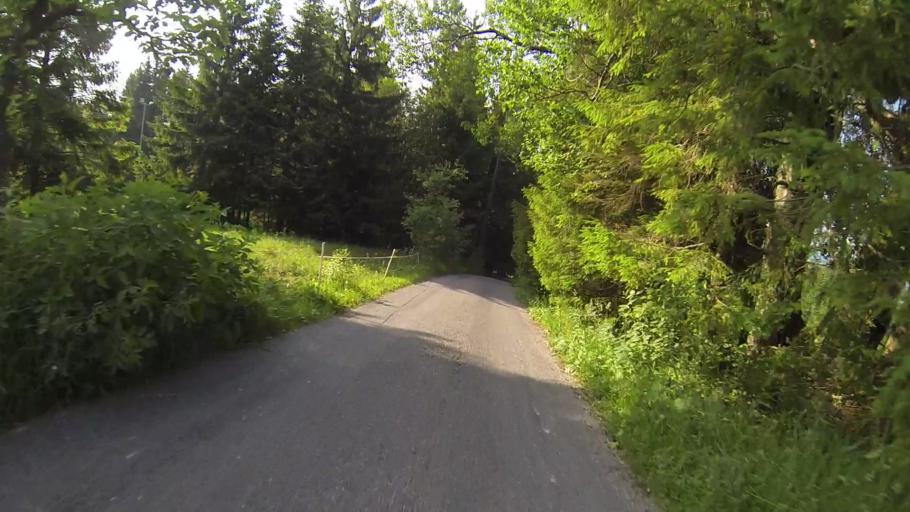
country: DE
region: Bavaria
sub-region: Swabia
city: Nesselwang
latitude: 47.6088
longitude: 10.4989
